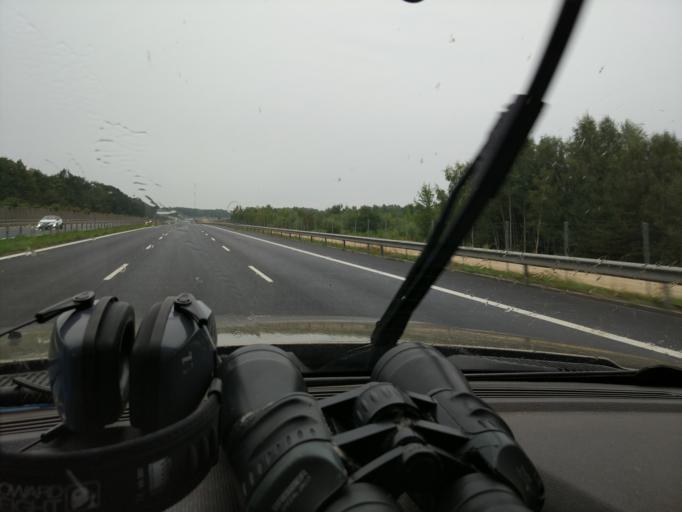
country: PL
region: Masovian Voivodeship
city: Zielonka
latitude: 52.3362
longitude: 21.1569
